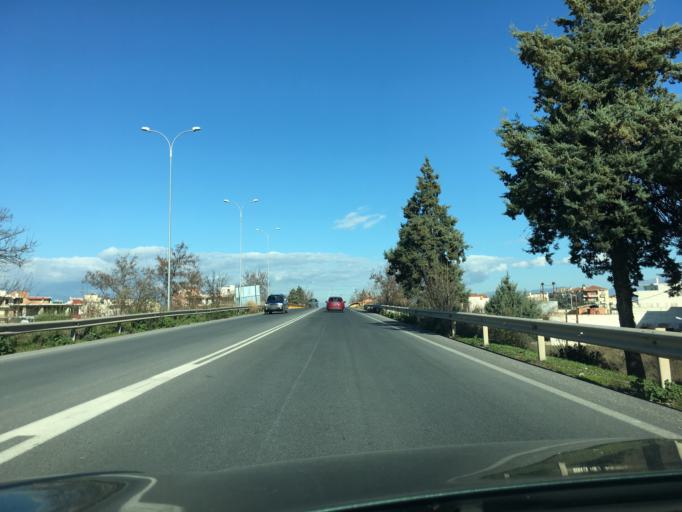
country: GR
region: Thessaly
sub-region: Nomos Larisis
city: Larisa
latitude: 39.6300
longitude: 22.4335
